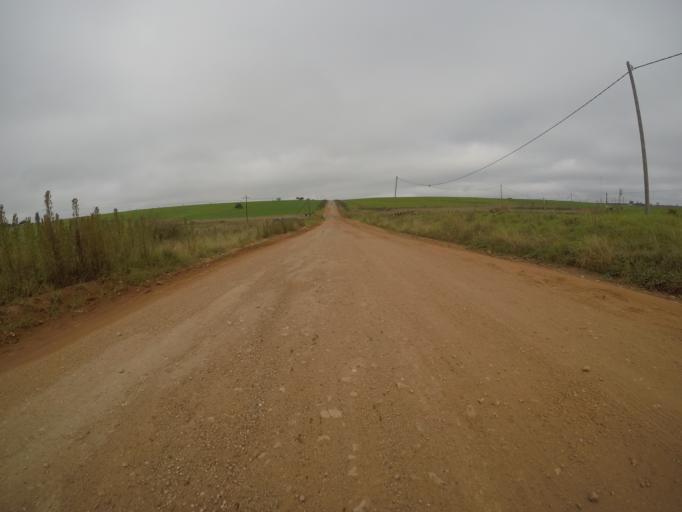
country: ZA
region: Eastern Cape
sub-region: Cacadu District Municipality
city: Kareedouw
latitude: -34.0179
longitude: 24.2390
